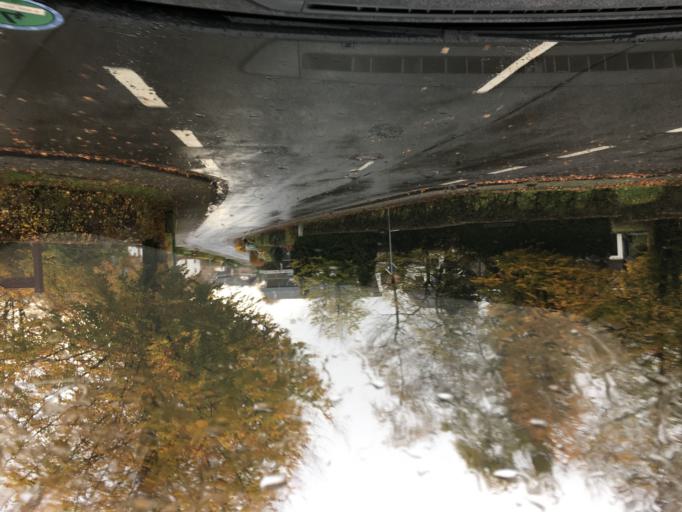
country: DE
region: North Rhine-Westphalia
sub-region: Regierungsbezirk Koln
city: Simmerath
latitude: 50.6282
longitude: 6.3515
